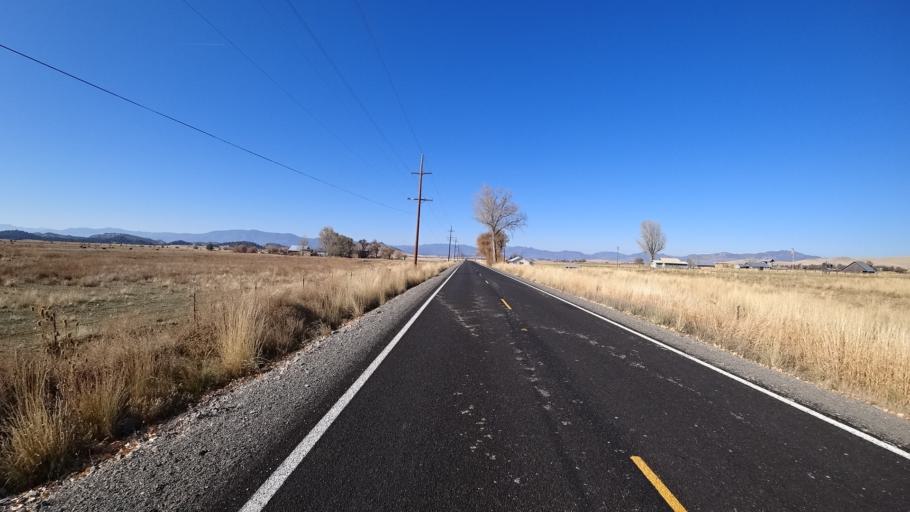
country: US
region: California
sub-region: Siskiyou County
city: Montague
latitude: 41.7114
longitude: -122.4120
